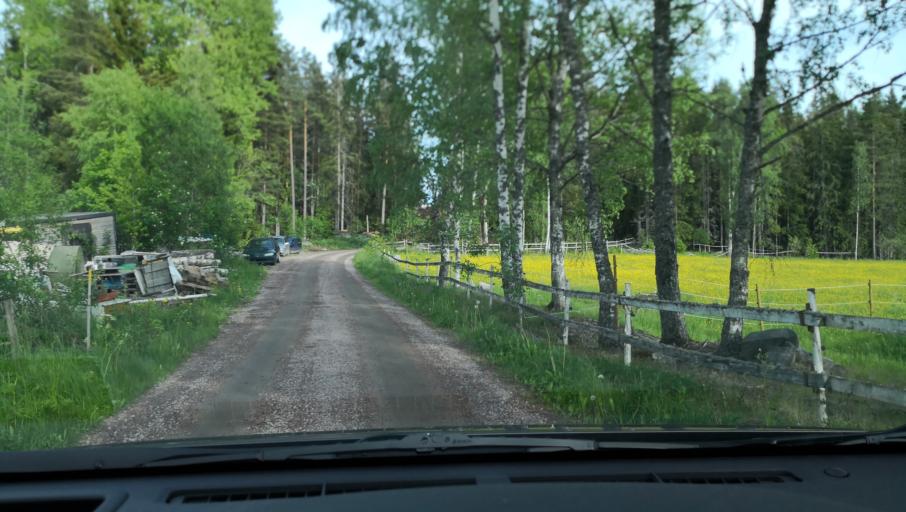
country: SE
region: Vaestmanland
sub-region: Kungsors Kommun
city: Kungsoer
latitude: 59.3604
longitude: 16.0264
